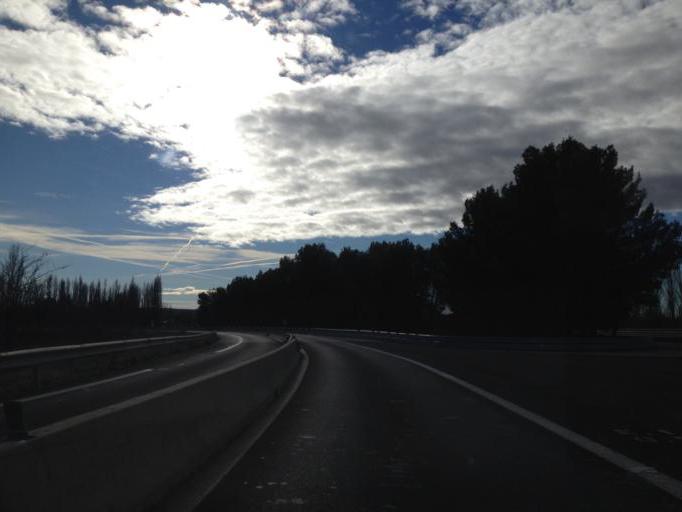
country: FR
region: Provence-Alpes-Cote d'Azur
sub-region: Departement du Vaucluse
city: Orange
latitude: 44.1301
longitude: 4.7901
